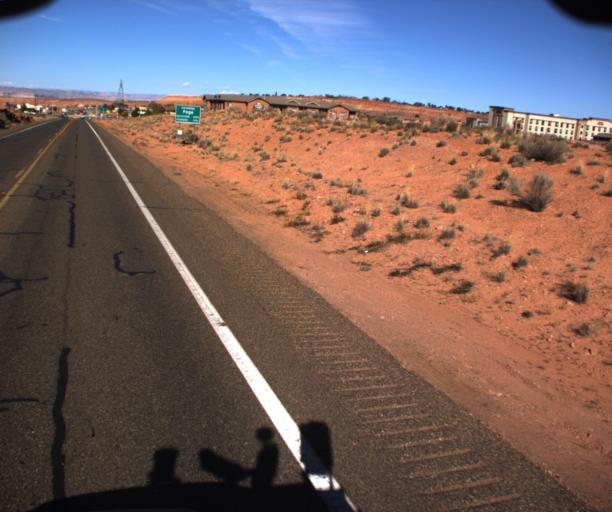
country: US
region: Arizona
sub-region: Coconino County
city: Page
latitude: 36.9011
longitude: -111.4865
